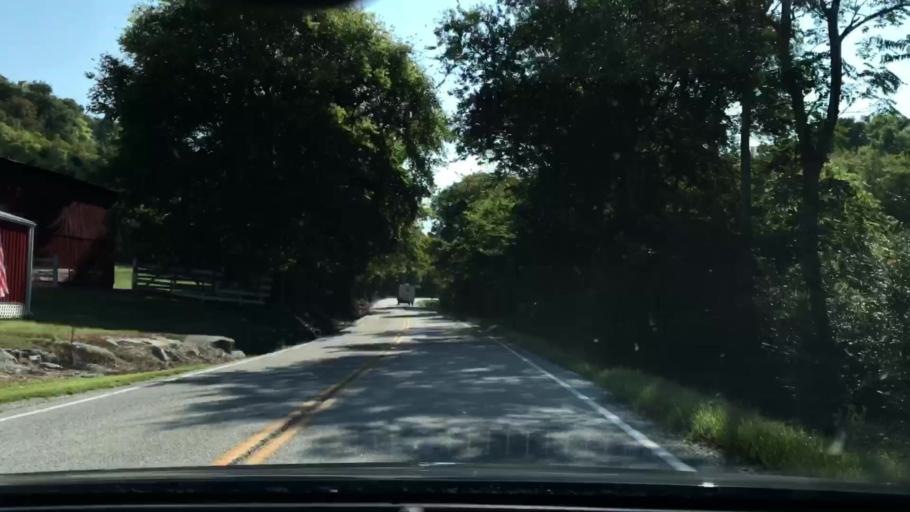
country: US
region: Tennessee
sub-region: Smith County
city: Carthage
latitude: 36.3519
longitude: -85.8903
